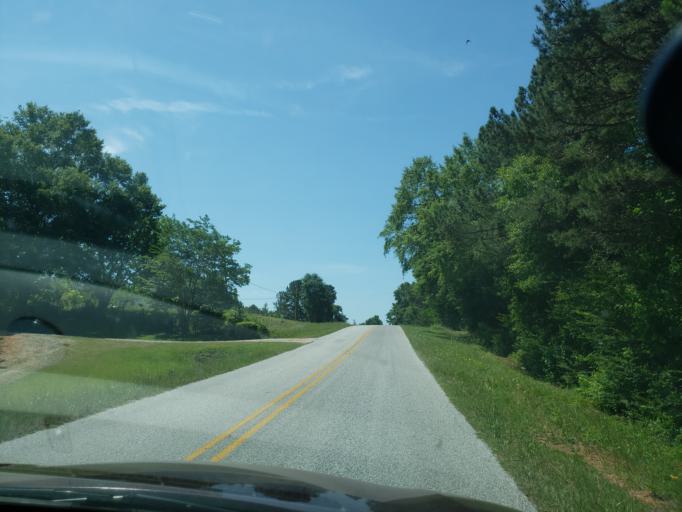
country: US
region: Alabama
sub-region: Elmore County
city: Tallassee
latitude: 32.5826
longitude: -85.8546
